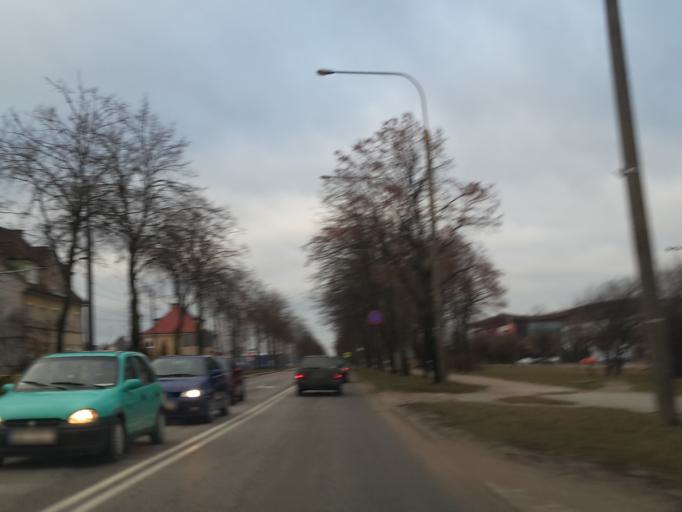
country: PL
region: Warmian-Masurian Voivodeship
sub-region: Powiat elblaski
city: Elblag
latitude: 54.1470
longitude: 19.4339
